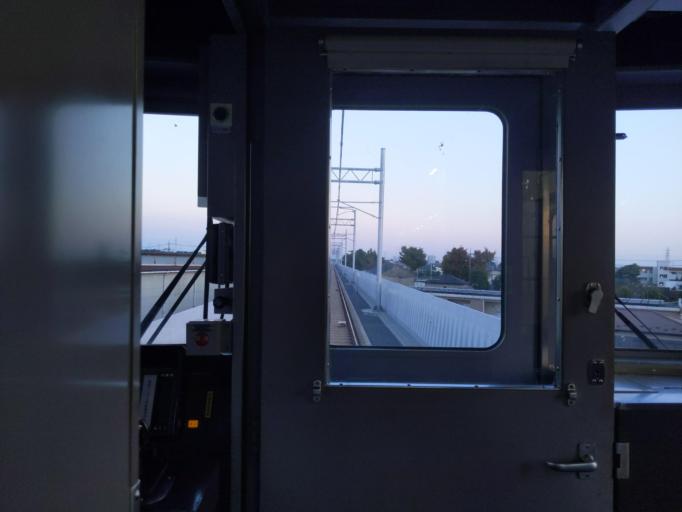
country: JP
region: Chiba
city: Noda
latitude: 35.9420
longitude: 139.8736
